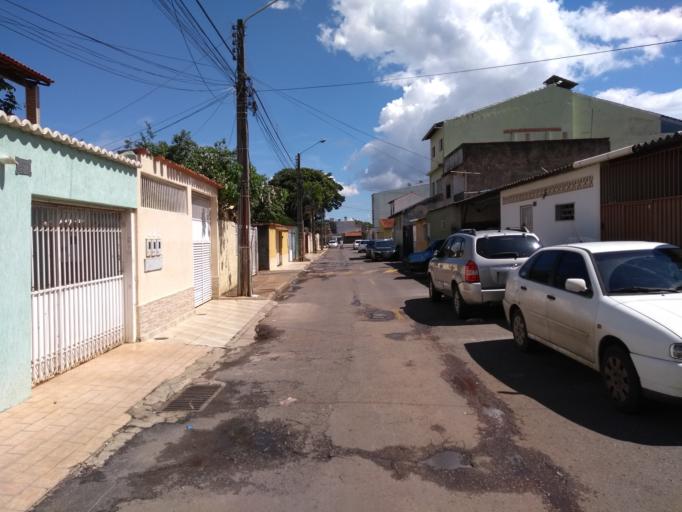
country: BR
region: Federal District
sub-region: Brasilia
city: Brasilia
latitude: -15.7903
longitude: -47.9405
